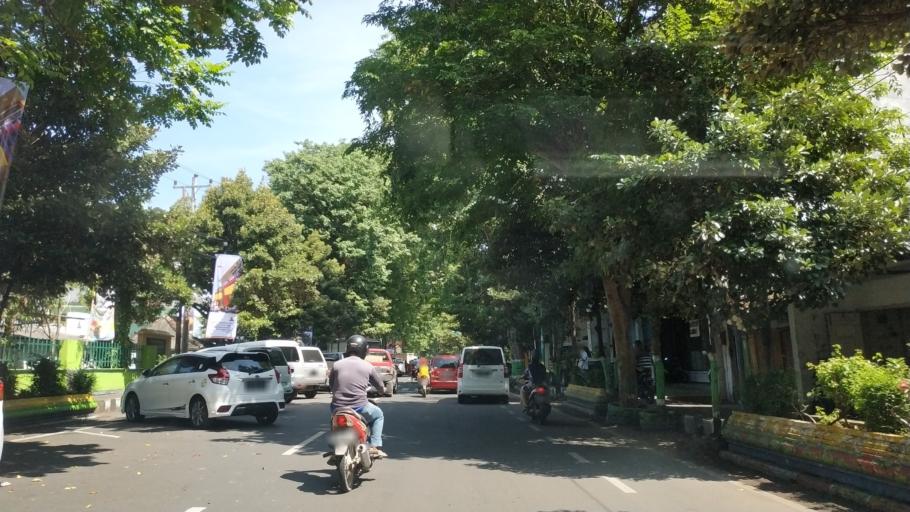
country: ID
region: Central Java
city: Pati
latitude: -6.7529
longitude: 111.0382
